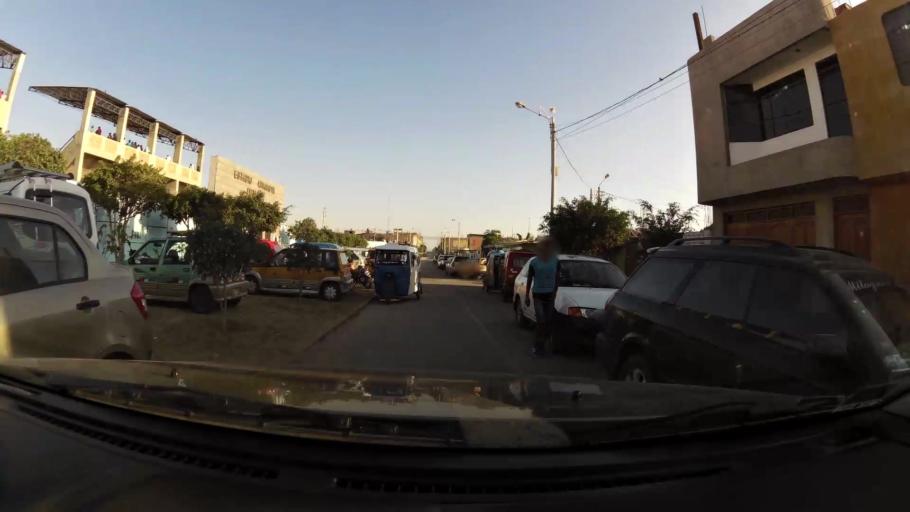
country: PE
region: Ica
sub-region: Provincia de Pisco
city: Villa Tupac Amaru
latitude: -13.7099
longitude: -76.1481
